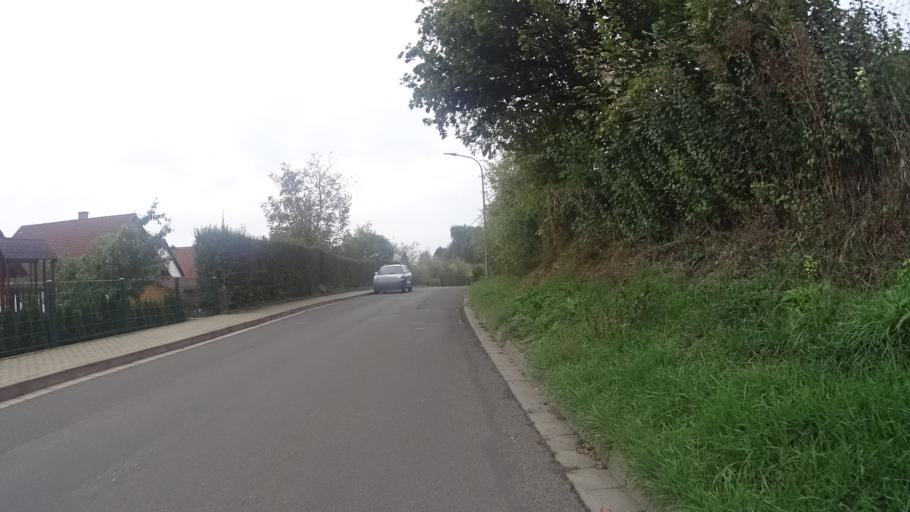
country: DE
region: Rheinland-Pfalz
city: Ottersheim
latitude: 49.6253
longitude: 8.1083
